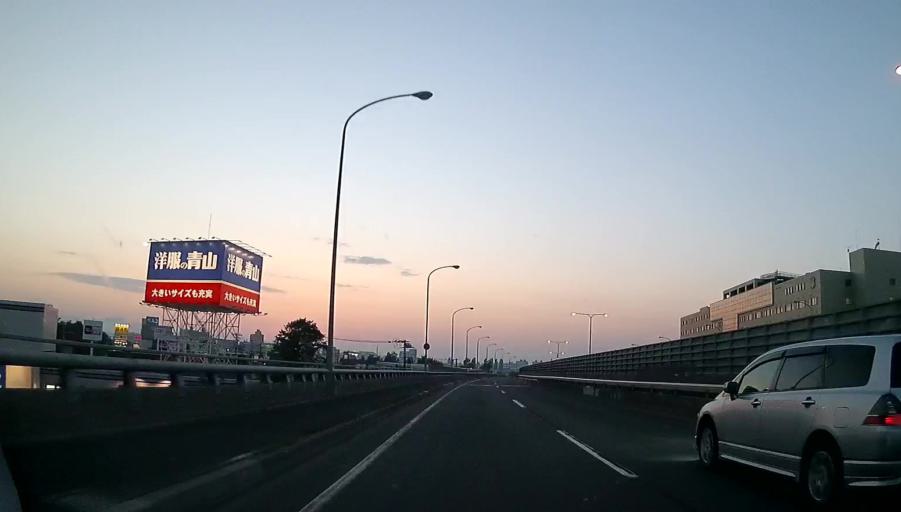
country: JP
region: Hokkaido
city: Sapporo
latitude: 43.0276
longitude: 141.4482
